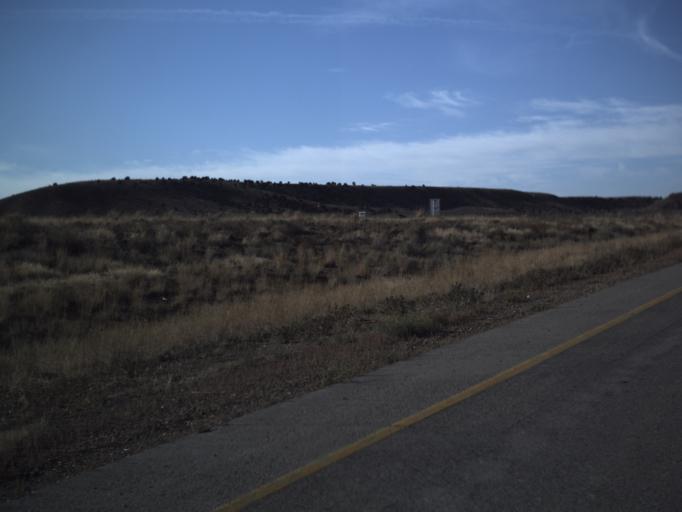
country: US
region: Utah
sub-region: Juab County
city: Nephi
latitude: 39.4826
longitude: -111.9807
